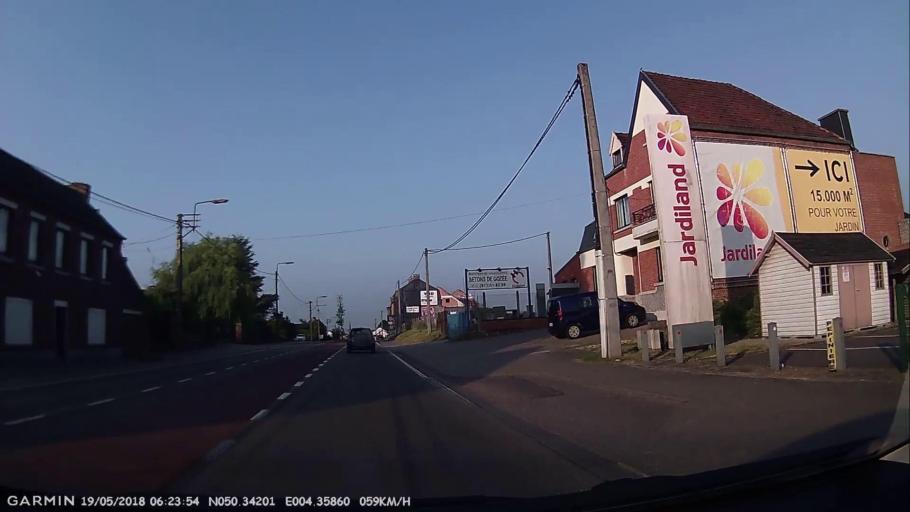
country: BE
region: Wallonia
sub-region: Province du Hainaut
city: Thuin
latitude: 50.3419
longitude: 4.3585
